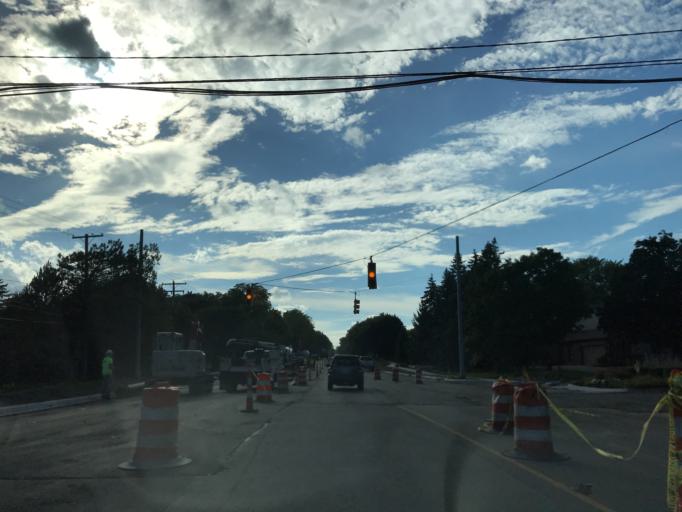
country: US
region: Michigan
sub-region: Oakland County
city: Farmington Hills
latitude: 42.5130
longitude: -83.3883
